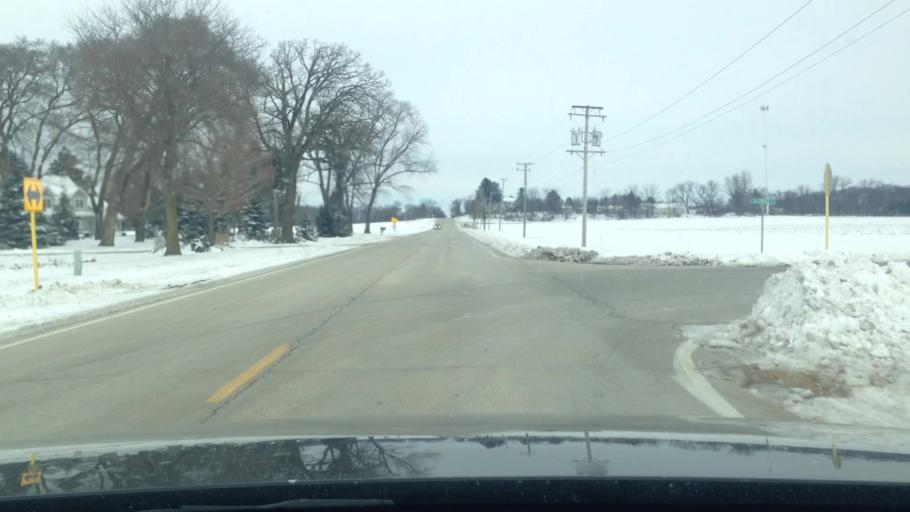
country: US
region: Illinois
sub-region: McHenry County
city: Hebron
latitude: 42.3994
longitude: -88.4382
